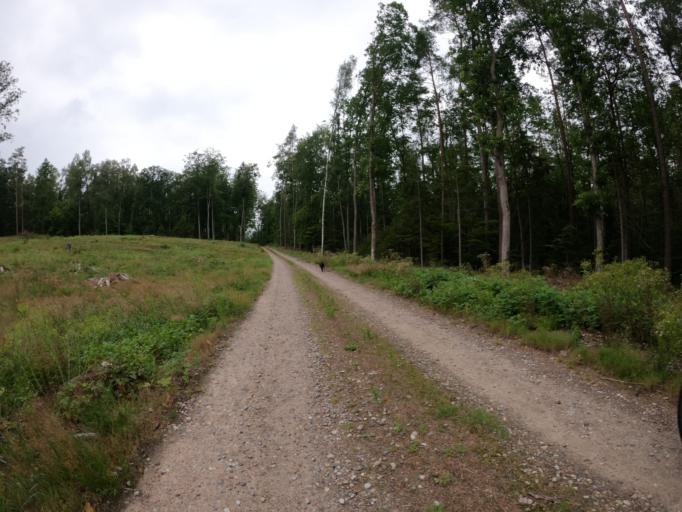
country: PL
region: West Pomeranian Voivodeship
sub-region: Powiat szczecinecki
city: Grzmiaca
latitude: 53.9768
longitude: 16.4200
